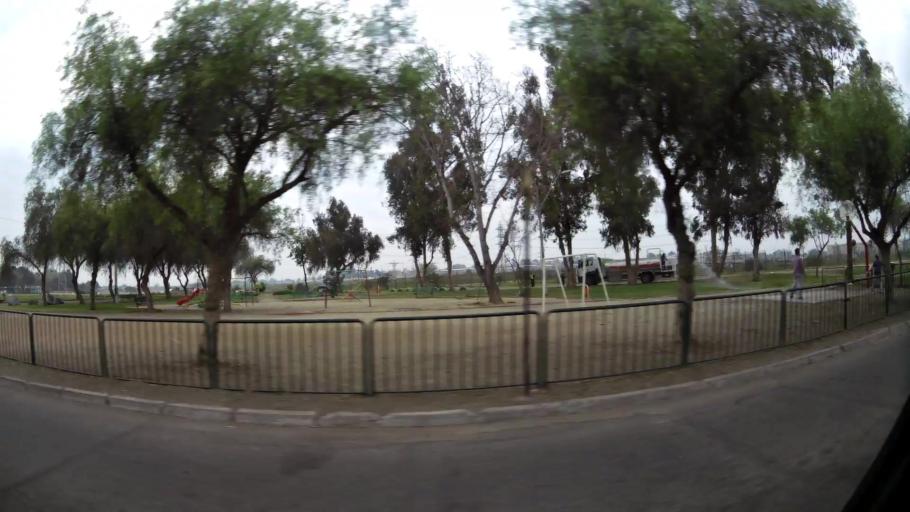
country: CL
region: Santiago Metropolitan
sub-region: Provincia de Santiago
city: Lo Prado
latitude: -33.4820
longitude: -70.7333
